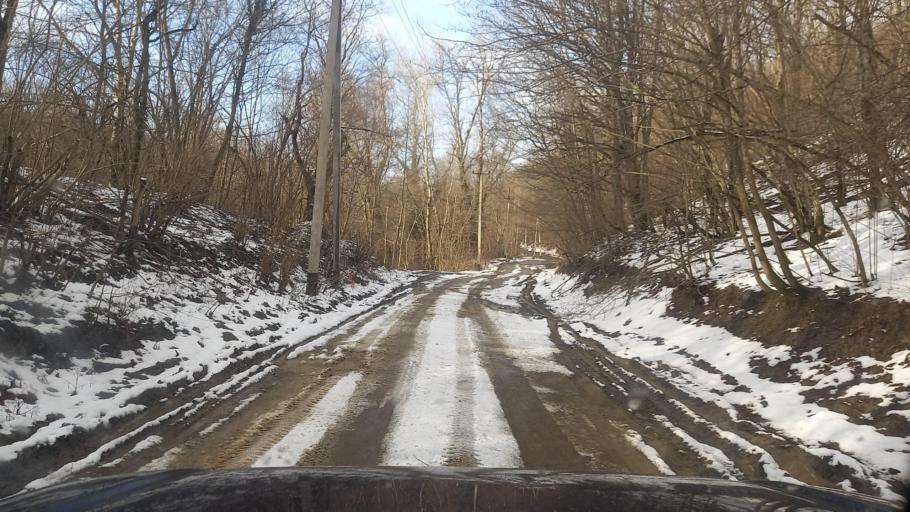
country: RU
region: Krasnodarskiy
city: Smolenskaya
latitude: 44.6988
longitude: 38.8285
